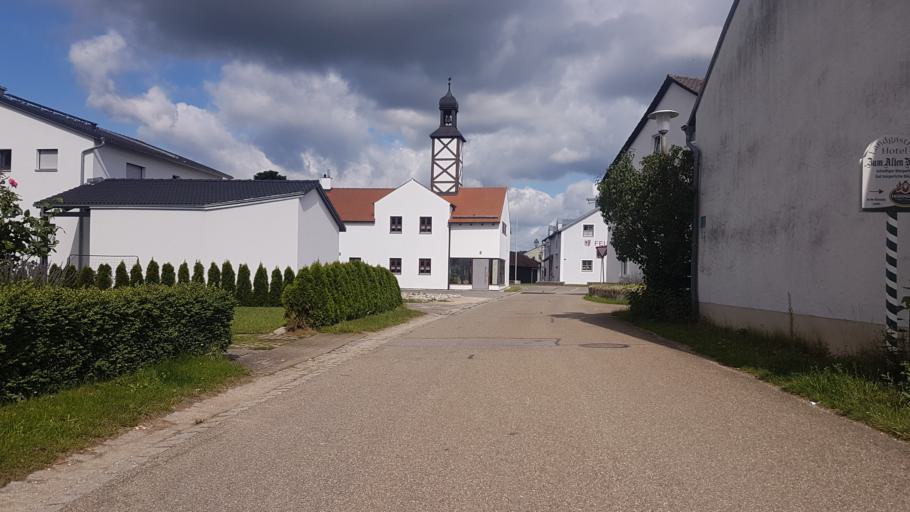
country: DE
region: Bavaria
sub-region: Upper Bavaria
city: Walting
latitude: 48.9230
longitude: 11.3500
